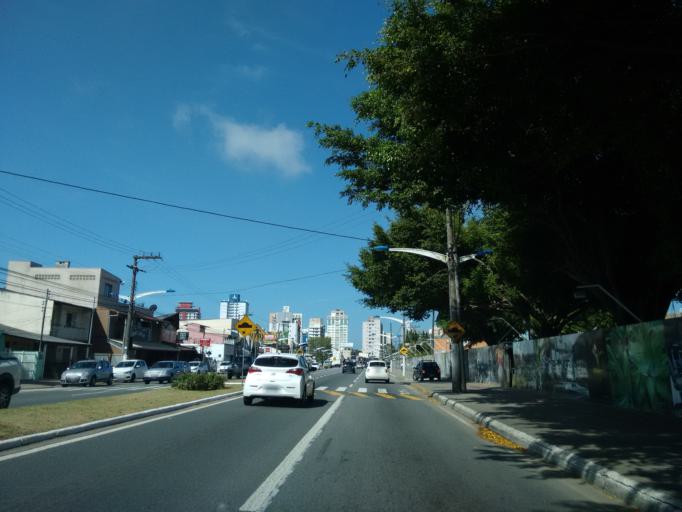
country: BR
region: Santa Catarina
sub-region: Itajai
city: Itajai
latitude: -26.9158
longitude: -48.6649
